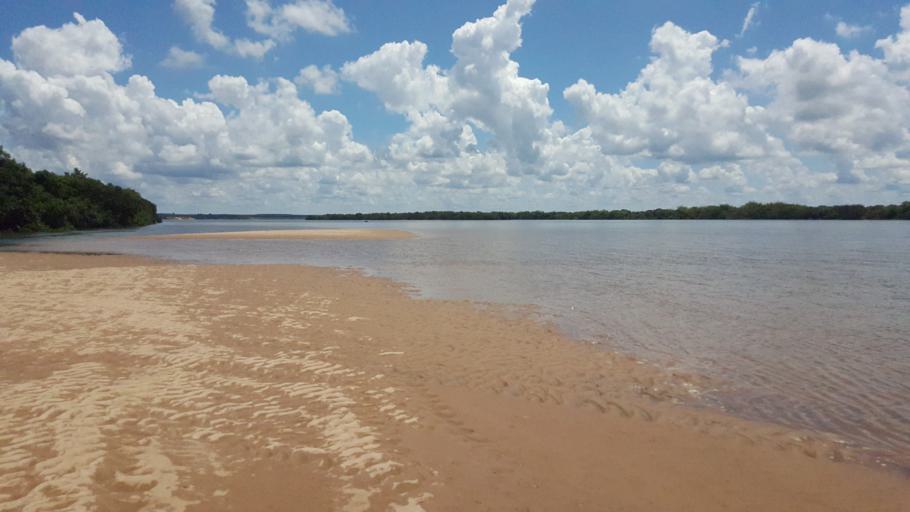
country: AR
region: Corrientes
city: Ituzaingo
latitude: -27.5746
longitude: -56.7061
